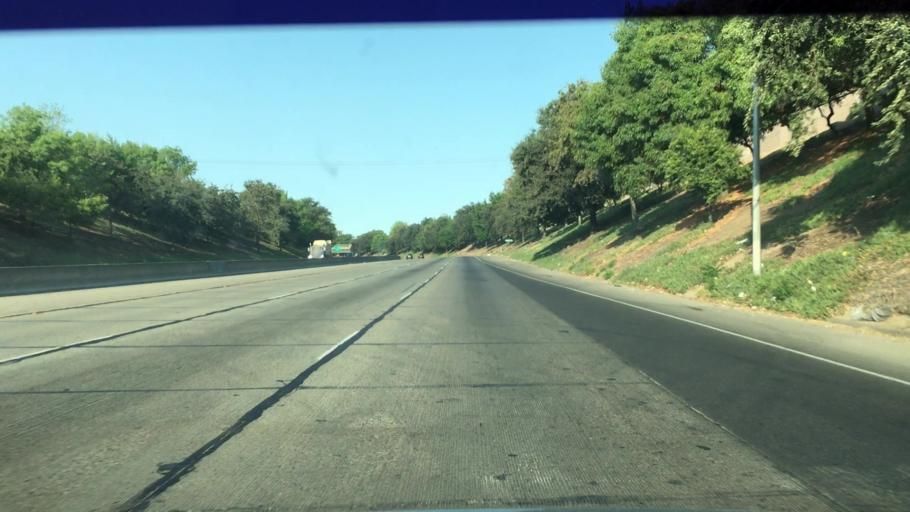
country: US
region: California
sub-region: San Joaquin County
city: August
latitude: 37.9584
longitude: -121.2591
